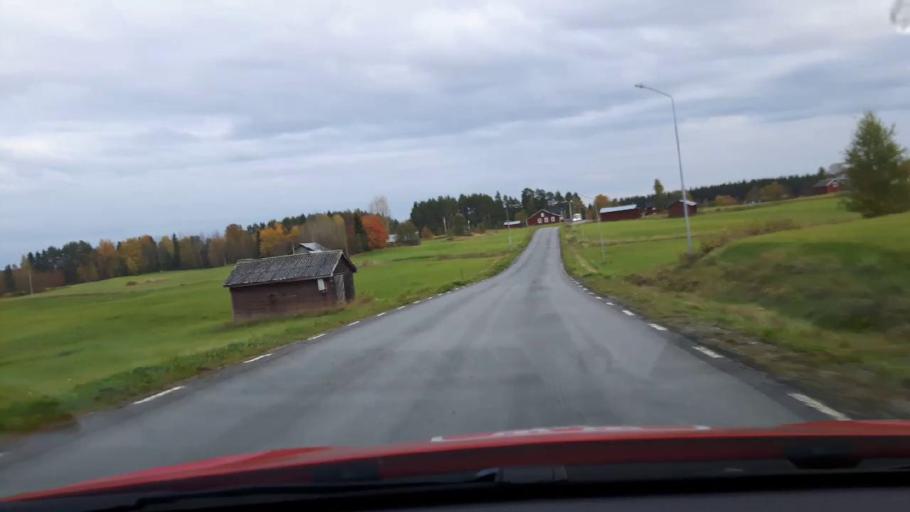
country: SE
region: Jaemtland
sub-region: OEstersunds Kommun
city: Lit
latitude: 63.3124
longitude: 14.9912
